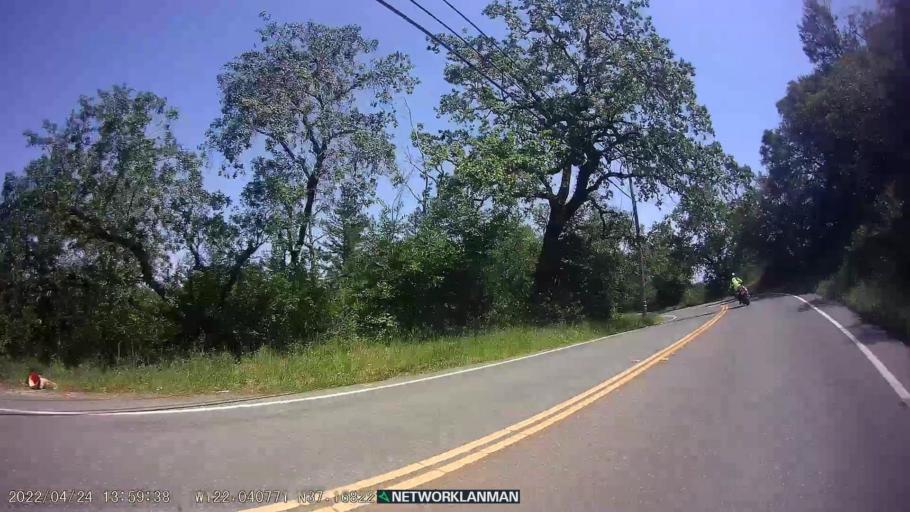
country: US
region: California
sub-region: Santa Cruz County
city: Lompico
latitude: 37.1681
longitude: -122.0405
